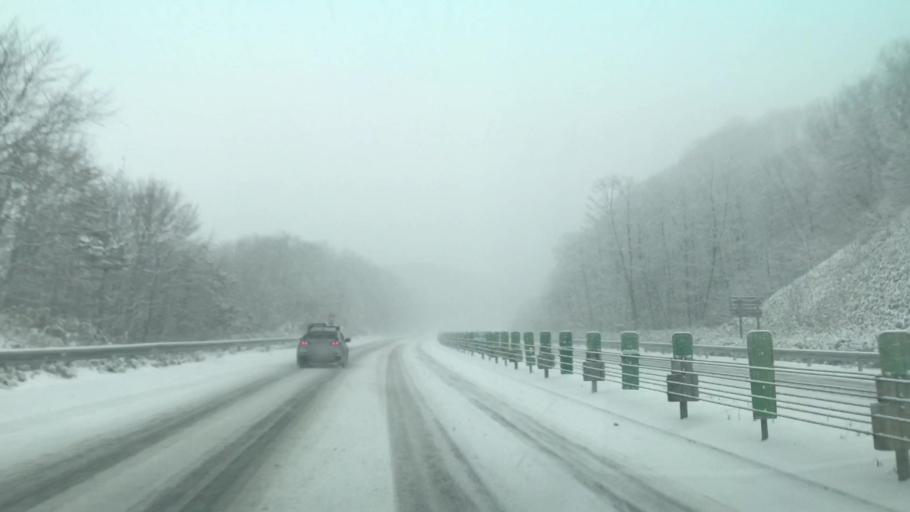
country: JP
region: Hokkaido
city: Shiraoi
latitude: 42.4988
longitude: 141.2613
